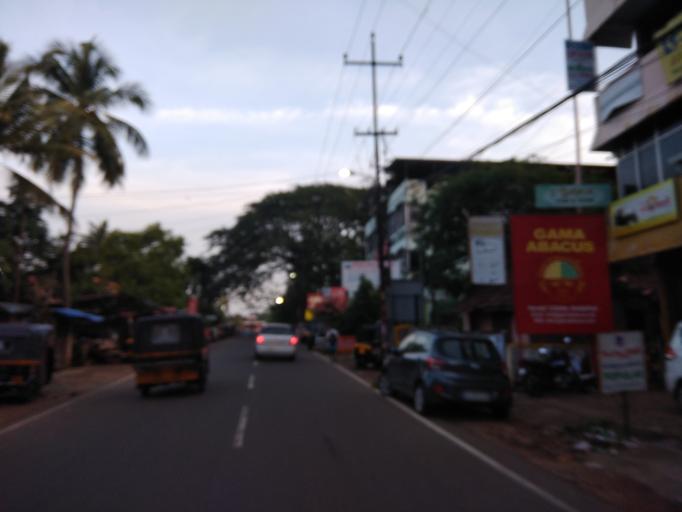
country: IN
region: Kerala
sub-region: Thrissur District
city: Trichur
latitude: 10.5213
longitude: 76.2022
